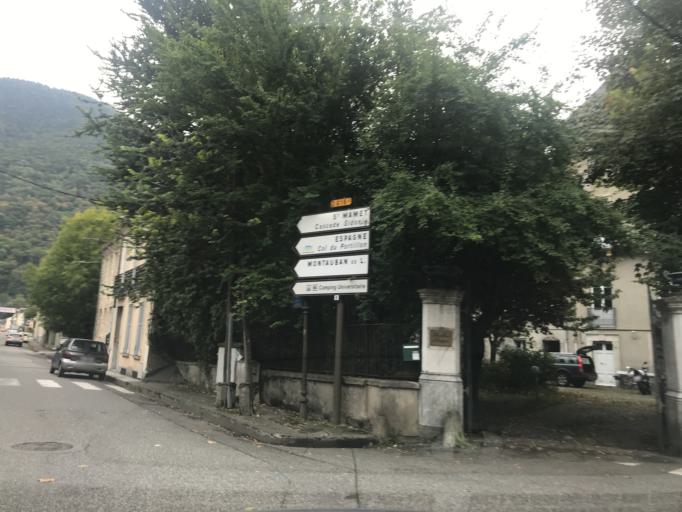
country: FR
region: Midi-Pyrenees
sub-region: Departement de la Haute-Garonne
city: Bagneres-de-Luchon
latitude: 42.7827
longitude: 0.5969
